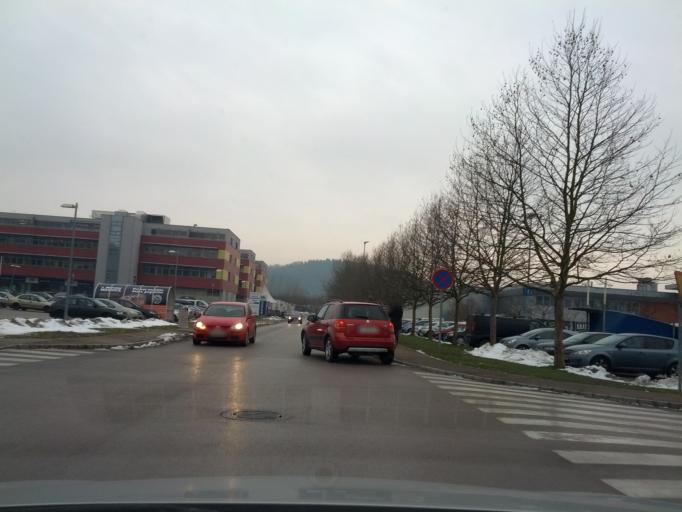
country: SI
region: Skofljica
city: Lavrica
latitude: 46.0220
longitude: 14.5377
